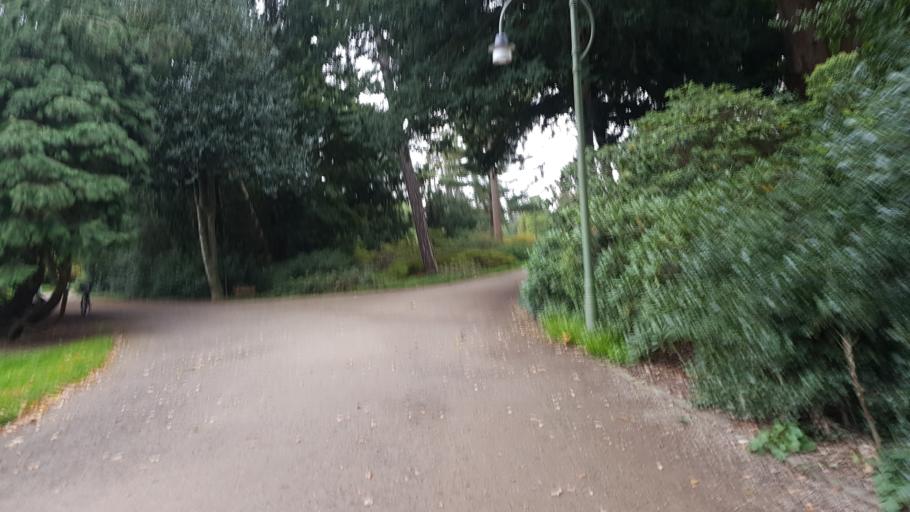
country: DE
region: Bremen
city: Bremen
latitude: 53.0888
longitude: 8.8258
